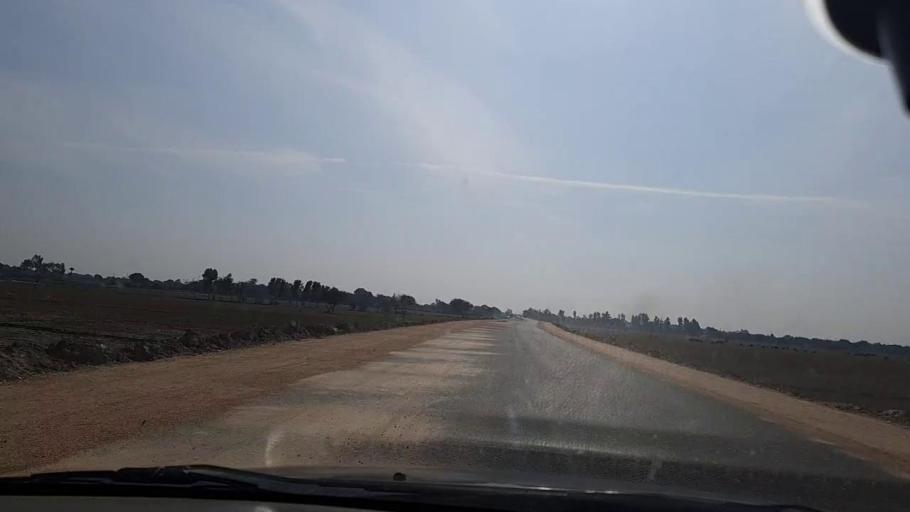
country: PK
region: Sindh
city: Mirpur Batoro
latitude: 24.7405
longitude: 68.2741
